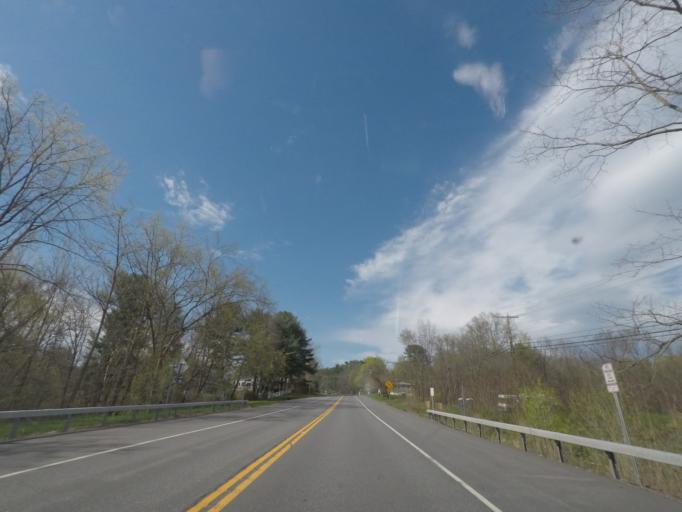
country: US
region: New York
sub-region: Greene County
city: Cairo
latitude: 42.3214
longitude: -74.0128
